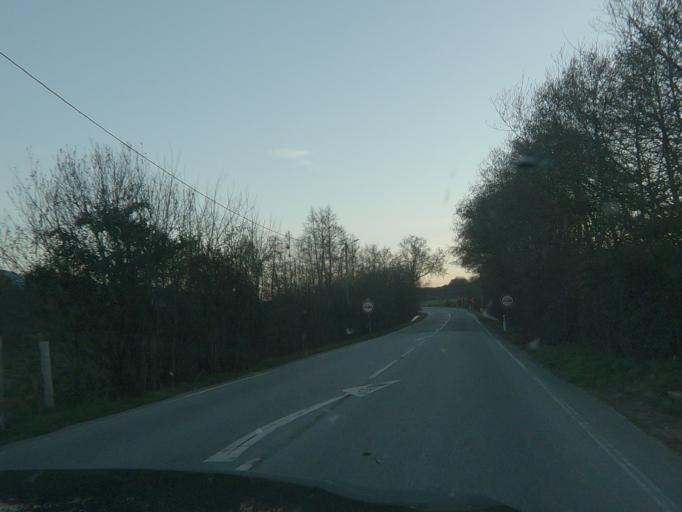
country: PT
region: Vila Real
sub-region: Vila Pouca de Aguiar
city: Vila Pouca de Aguiar
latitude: 41.4680
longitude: -7.6645
